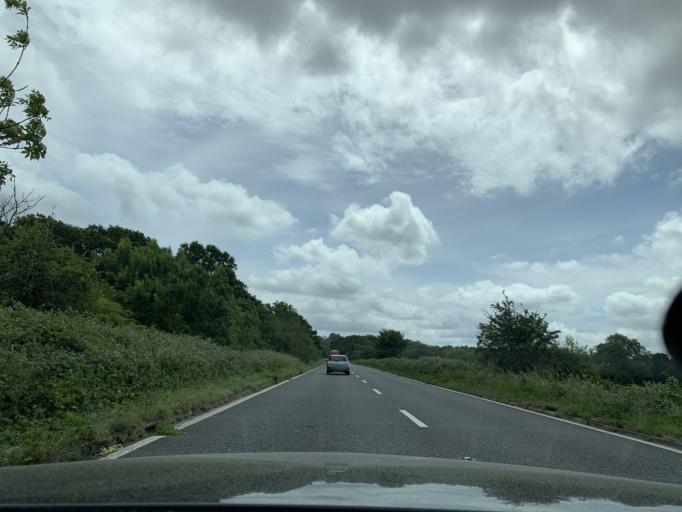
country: GB
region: England
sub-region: East Sussex
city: Robertsbridge
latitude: 50.9734
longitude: 0.4759
